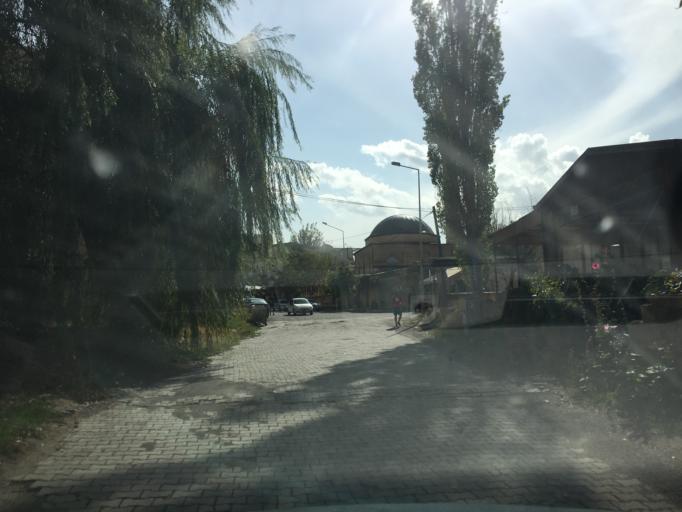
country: TR
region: Nevsehir
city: Goereme
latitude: 38.6678
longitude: 34.8420
